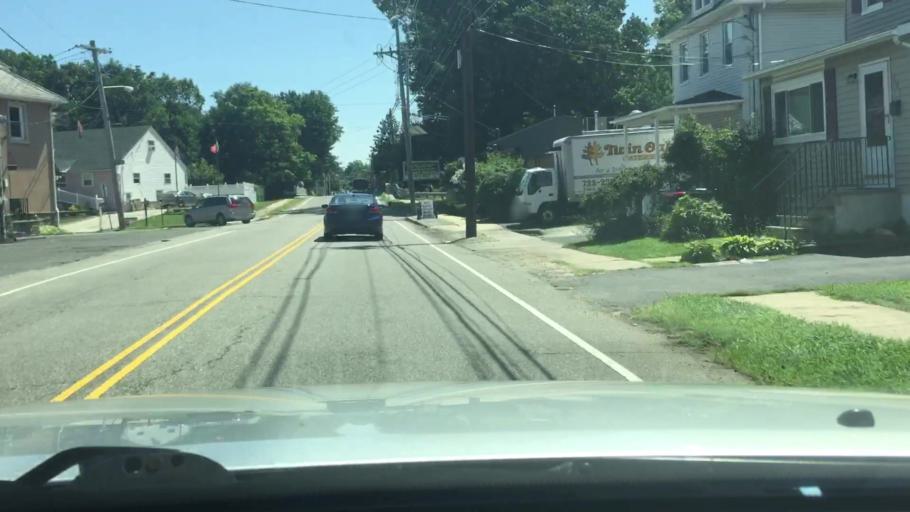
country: US
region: New Jersey
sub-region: Middlesex County
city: South River
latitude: 40.4445
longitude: -74.3934
